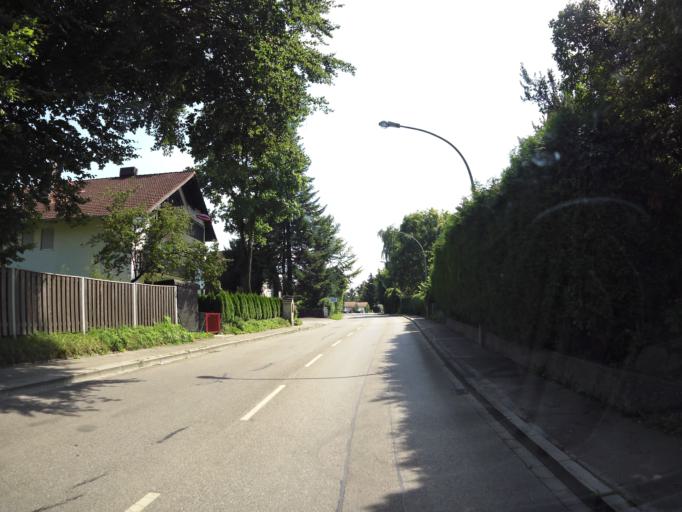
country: DE
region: Bavaria
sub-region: Upper Bavaria
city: Diessen am Ammersee
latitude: 47.9445
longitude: 11.1051
